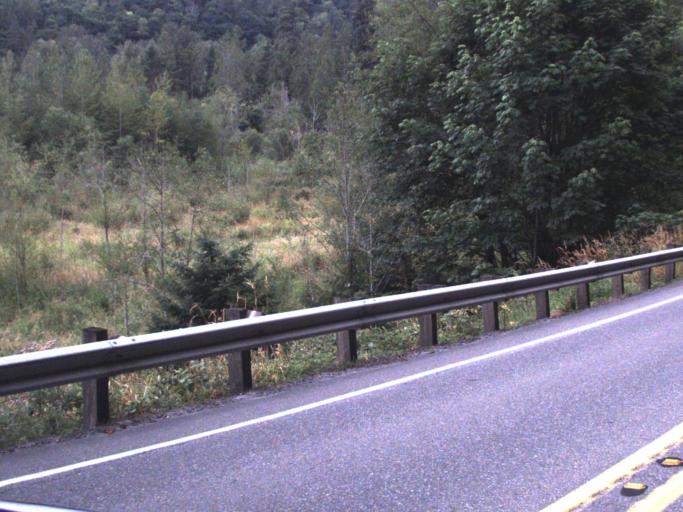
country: US
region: Washington
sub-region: King County
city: Ames Lake
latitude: 47.6280
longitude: -121.9889
